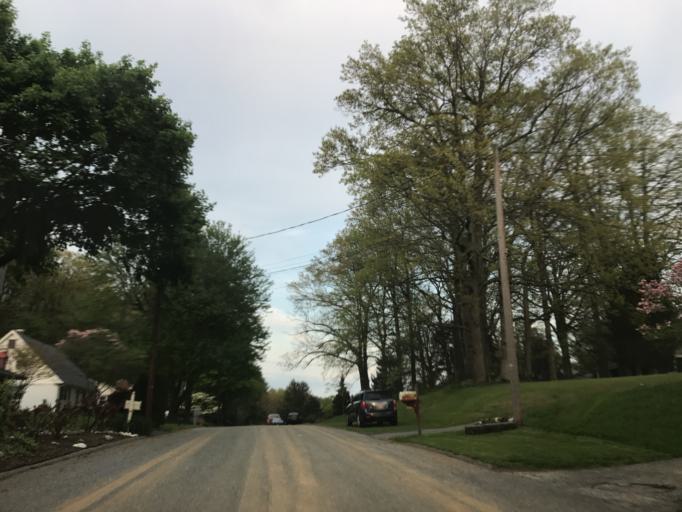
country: US
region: Maryland
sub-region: Baltimore County
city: Cockeysville
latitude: 39.4775
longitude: -76.6335
